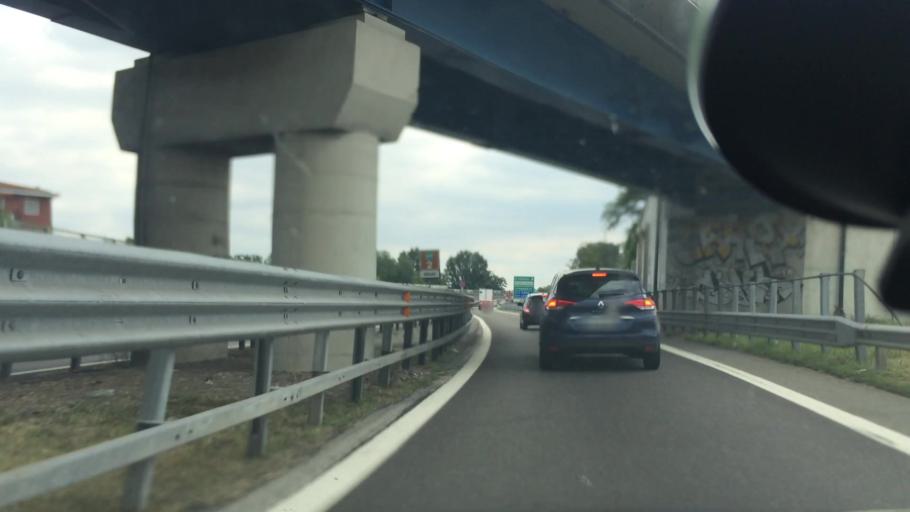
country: IT
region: Lombardy
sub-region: Citta metropolitana di Milano
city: Rho
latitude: 45.5157
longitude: 9.0605
